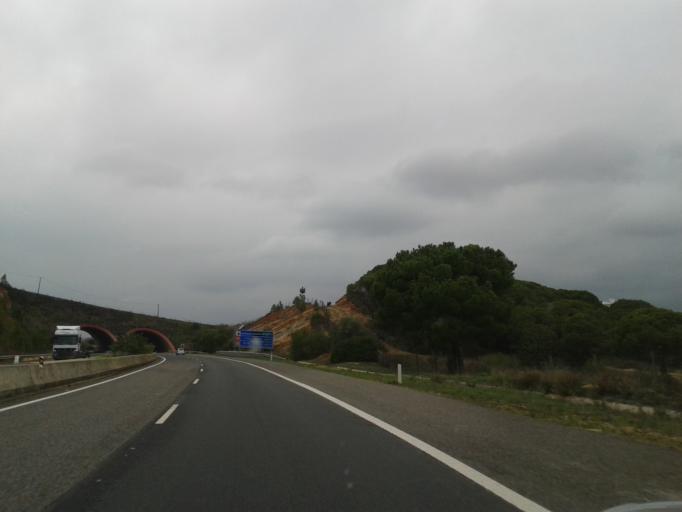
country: PT
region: Faro
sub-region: Silves
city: Armacao de Pera
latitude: 37.1386
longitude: -8.3914
